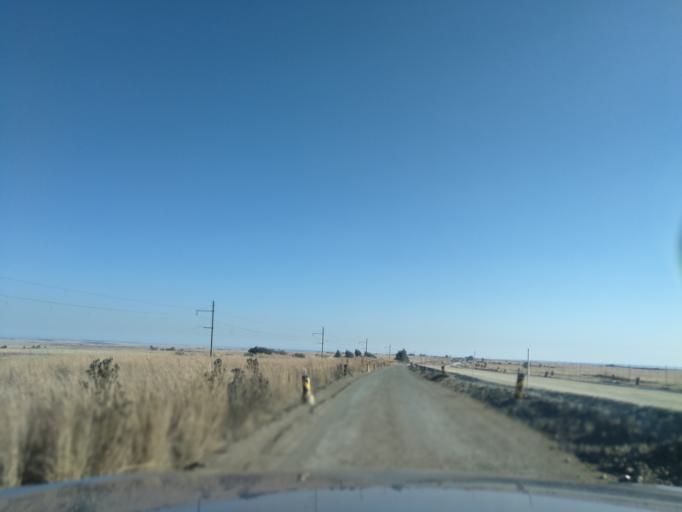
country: ZA
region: Orange Free State
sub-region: Fezile Dabi District Municipality
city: Kroonstad
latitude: -27.8778
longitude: 27.4392
